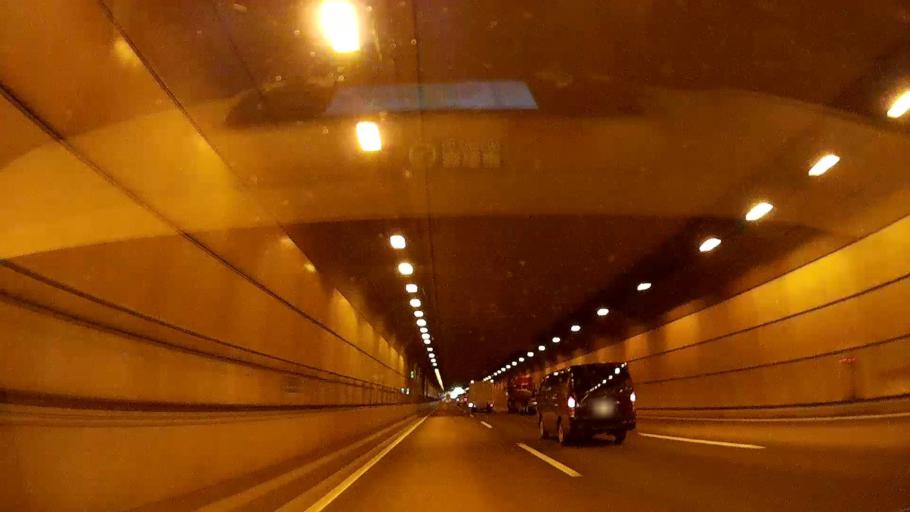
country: JP
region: Kanagawa
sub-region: Kawasaki-shi
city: Kawasaki
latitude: 35.5620
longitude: 139.7737
